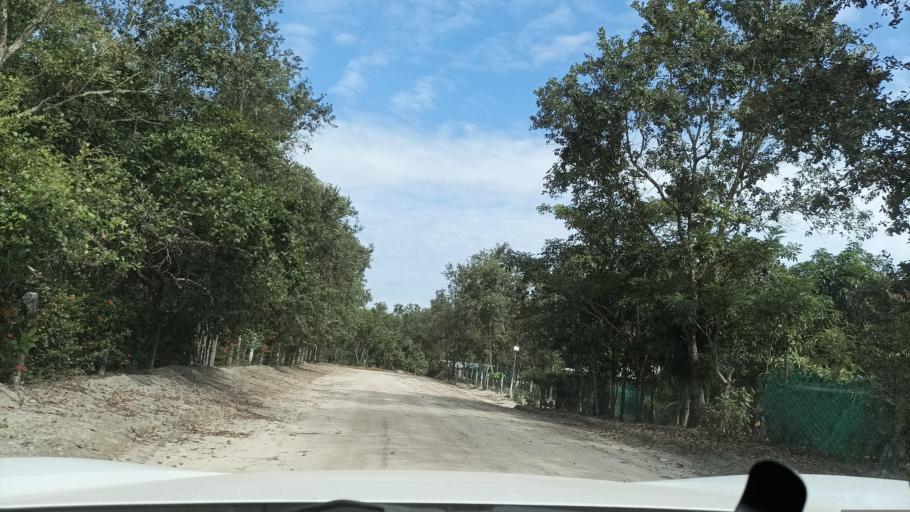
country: MX
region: Veracruz
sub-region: Cosoleacaque
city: Coacotla
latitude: 17.9460
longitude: -94.7098
